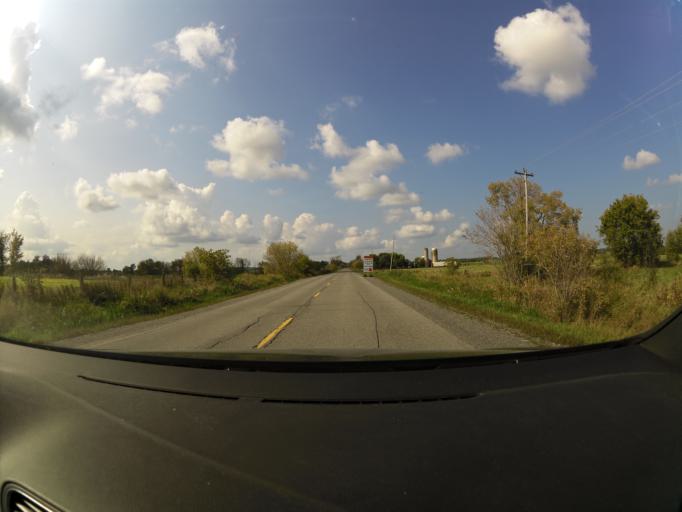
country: CA
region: Ontario
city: Arnprior
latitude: 45.3792
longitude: -76.1724
